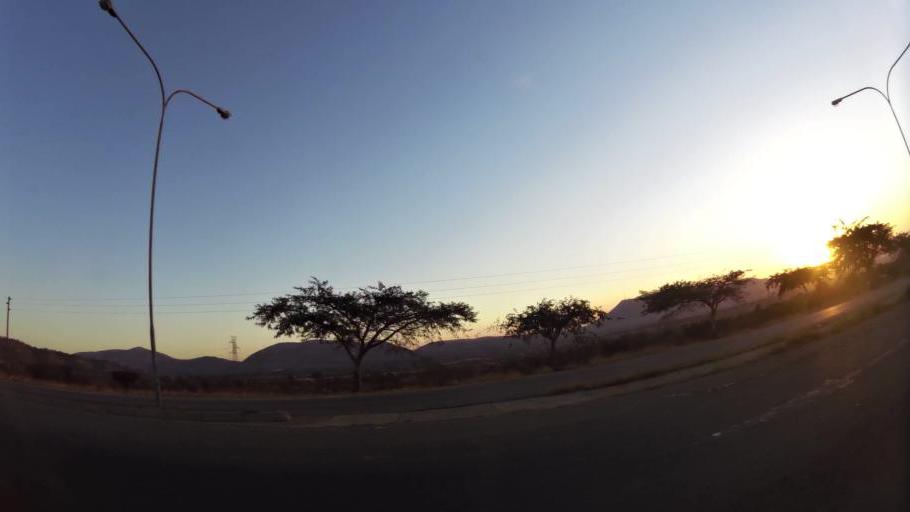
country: ZA
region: North-West
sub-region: Bojanala Platinum District Municipality
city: Rustenburg
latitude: -25.6156
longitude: 27.1792
